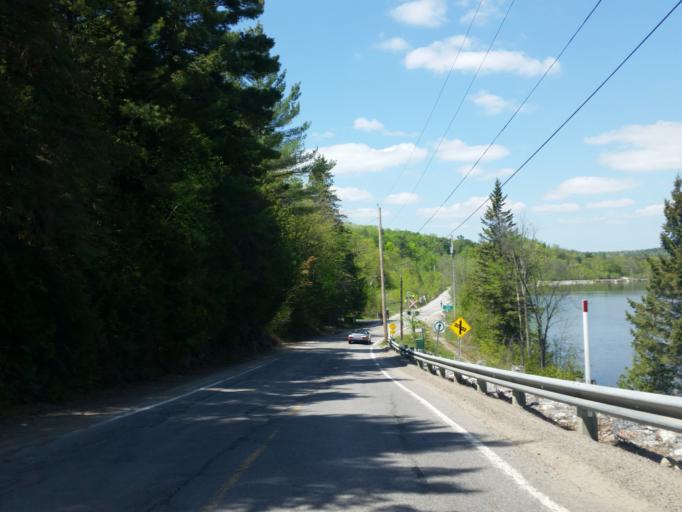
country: CA
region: Quebec
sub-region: Outaouais
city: Wakefield
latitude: 45.5937
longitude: -75.8749
